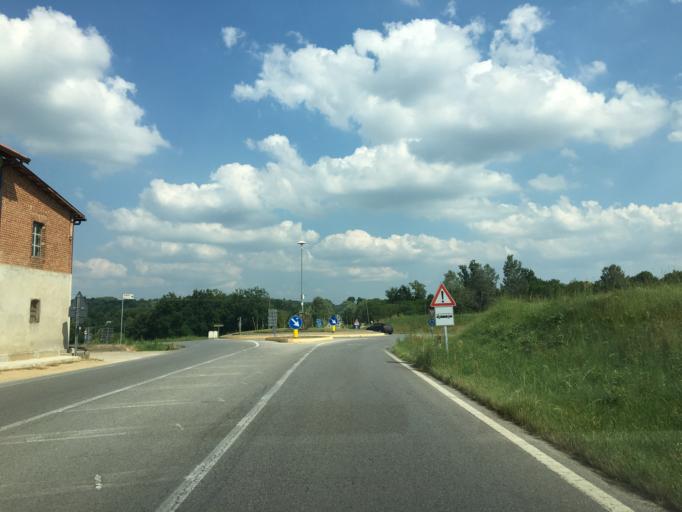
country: IT
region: Piedmont
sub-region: Provincia di Cuneo
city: Ceresole Alba
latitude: 44.7836
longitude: 7.8638
